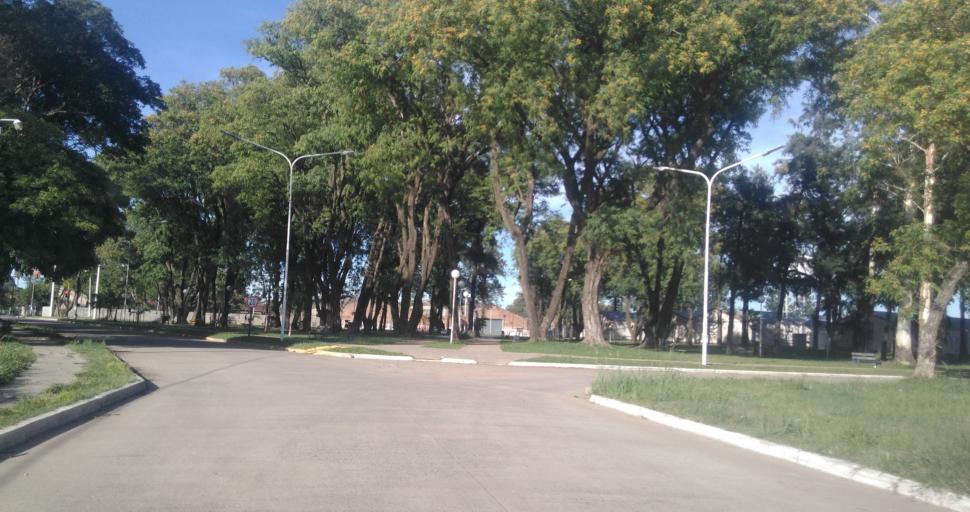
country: AR
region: Chaco
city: Fontana
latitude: -27.4154
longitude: -59.0297
